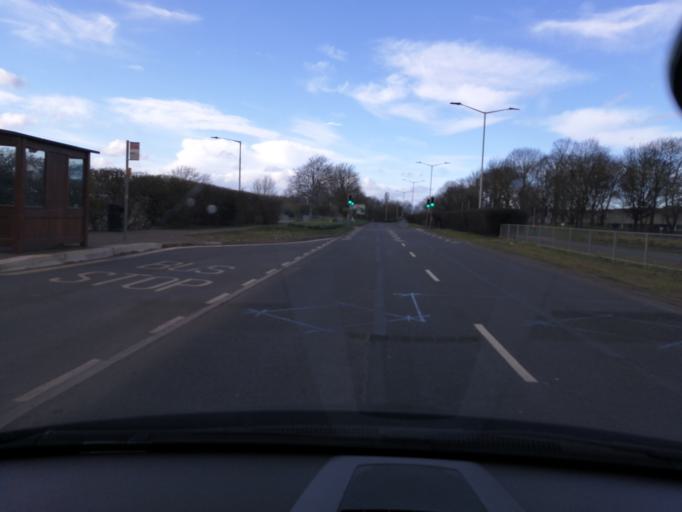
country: GB
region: England
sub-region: Peterborough
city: Peterborough
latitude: 52.5934
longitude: -0.2681
